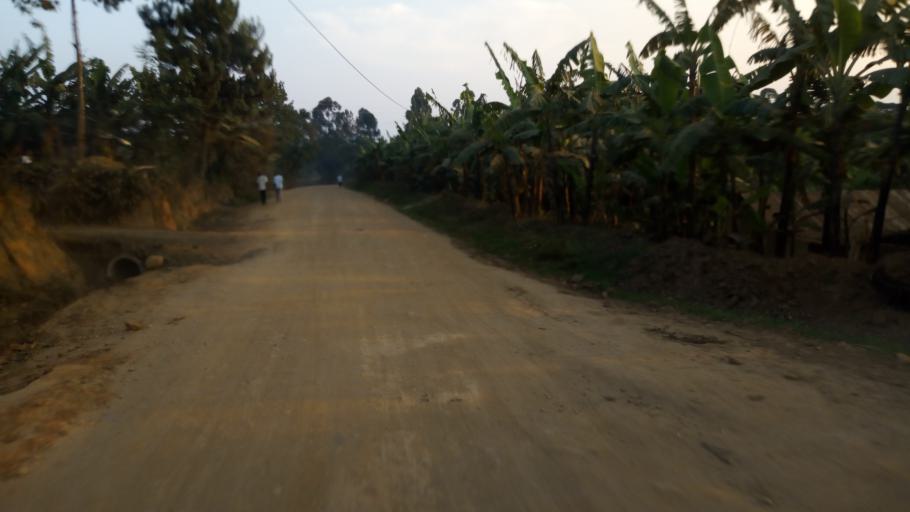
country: UG
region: Western Region
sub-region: Rukungiri District
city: Rukungiri
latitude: -0.7686
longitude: 29.9269
